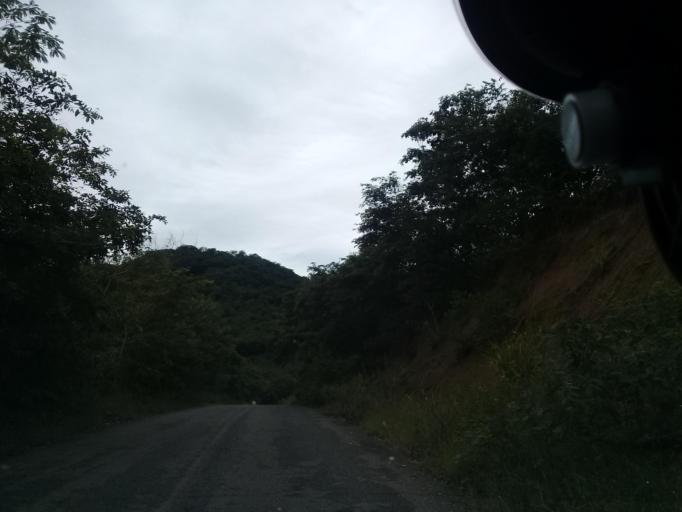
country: MX
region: Hidalgo
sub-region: Huejutla de Reyes
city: Chalahuiyapa
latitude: 21.2002
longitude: -98.3475
